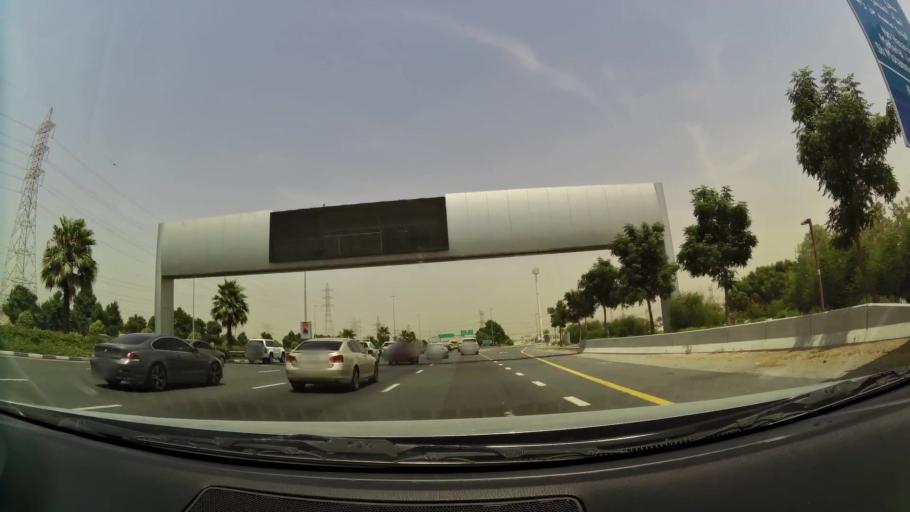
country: AE
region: Ash Shariqah
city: Sharjah
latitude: 25.2124
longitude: 55.3938
